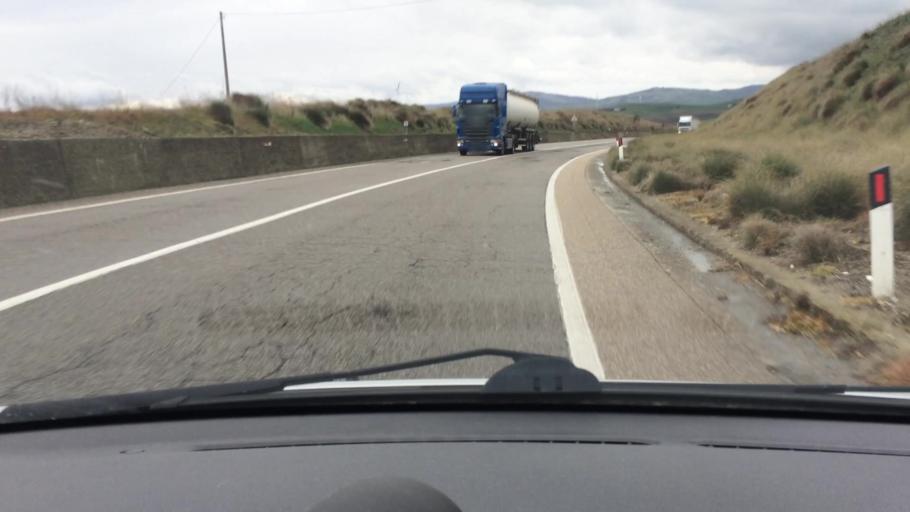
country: IT
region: Basilicate
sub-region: Provincia di Potenza
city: San Chirico Nuovo
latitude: 40.7751
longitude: 16.1289
